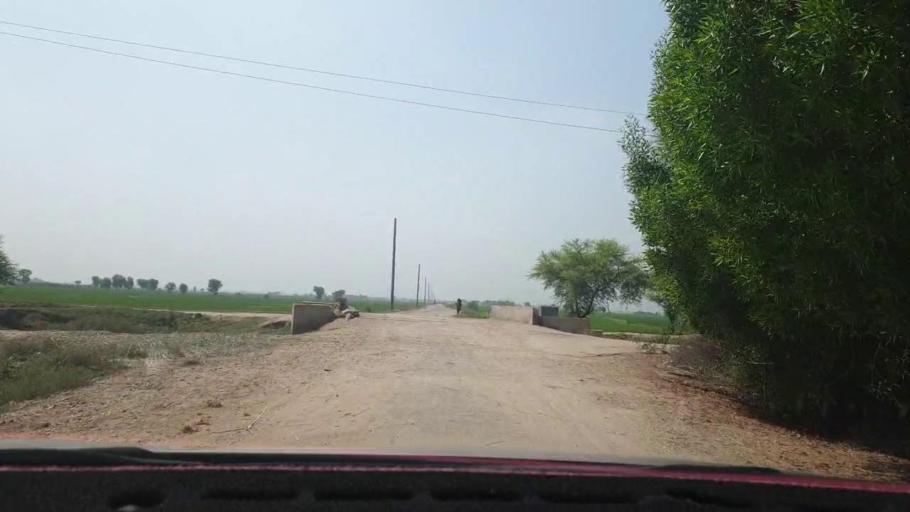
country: PK
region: Sindh
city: Warah
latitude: 27.4151
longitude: 67.8445
